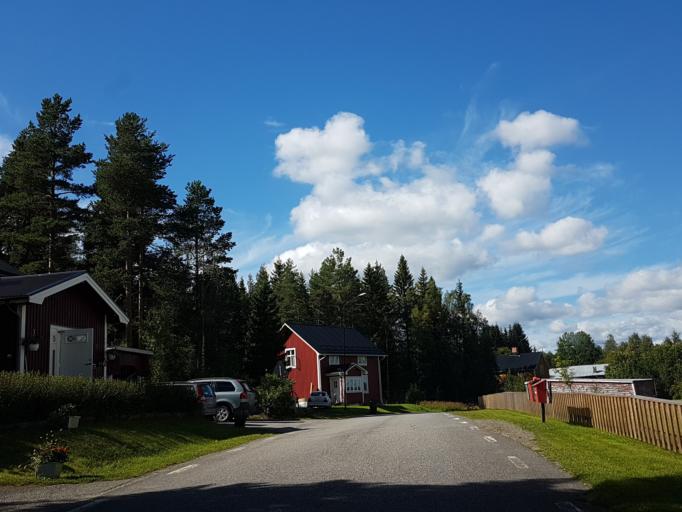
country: SE
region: Vaesterbotten
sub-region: Skelleftea Kommun
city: Burtraesk
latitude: 64.2689
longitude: 20.4924
